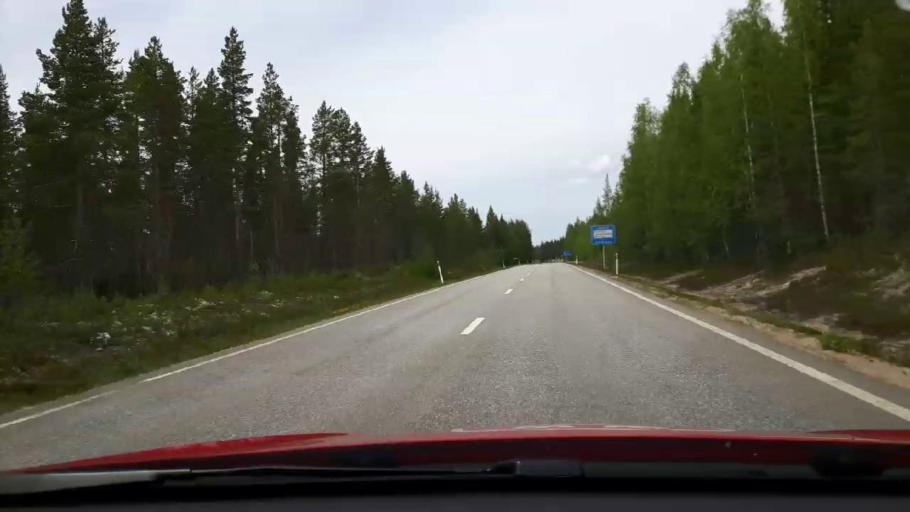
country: SE
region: Jaemtland
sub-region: Harjedalens Kommun
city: Sveg
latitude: 62.1167
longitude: 14.1745
